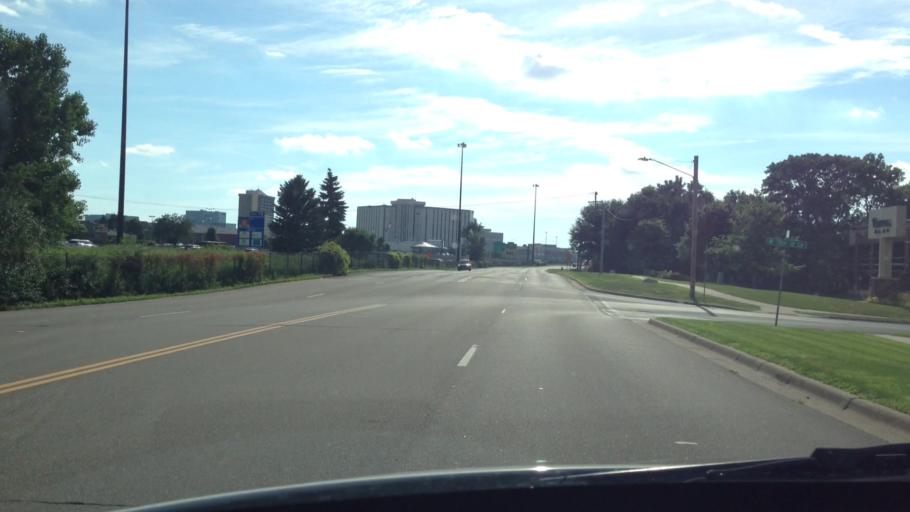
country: US
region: Minnesota
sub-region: Hennepin County
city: Edina
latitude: 44.8587
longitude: -93.3371
